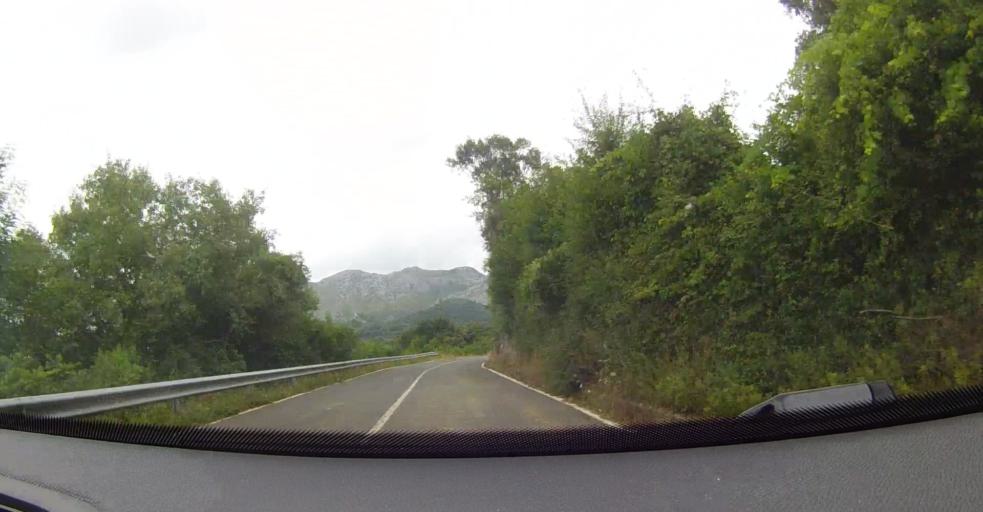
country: ES
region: Cantabria
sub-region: Provincia de Cantabria
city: Rasines
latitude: 43.2594
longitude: -3.3713
